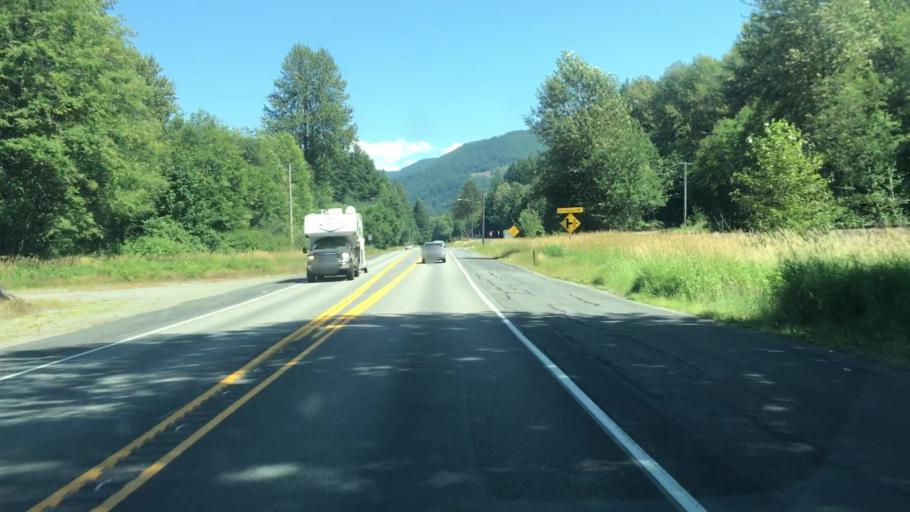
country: US
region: Washington
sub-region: Snohomish County
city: Gold Bar
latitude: 47.7135
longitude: -121.3375
